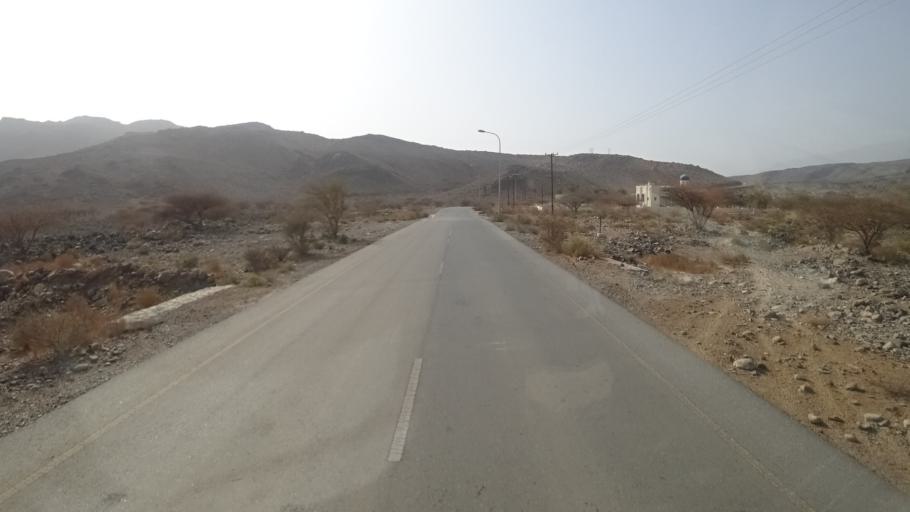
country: OM
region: Muhafazat ad Dakhiliyah
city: Bahla'
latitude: 23.0678
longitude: 57.3702
